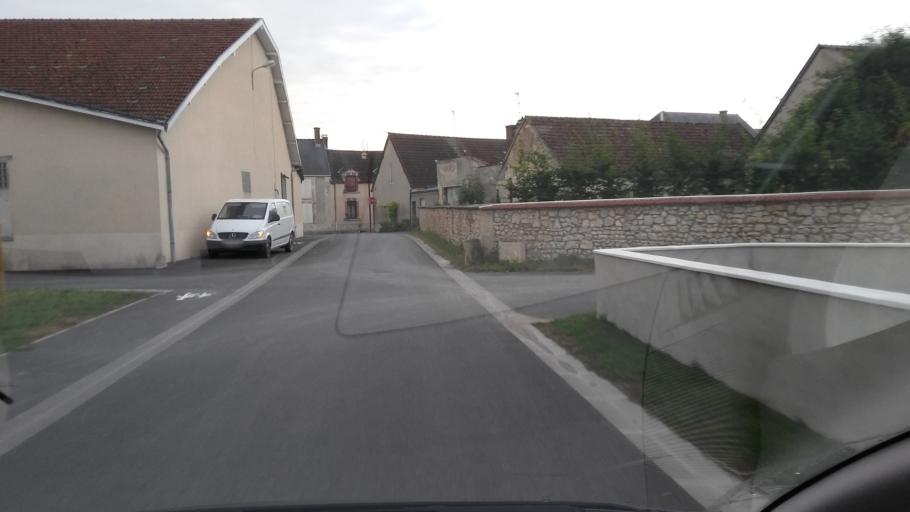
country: FR
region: Champagne-Ardenne
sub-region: Departement de la Marne
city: Vertus
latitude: 48.8796
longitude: 4.0022
